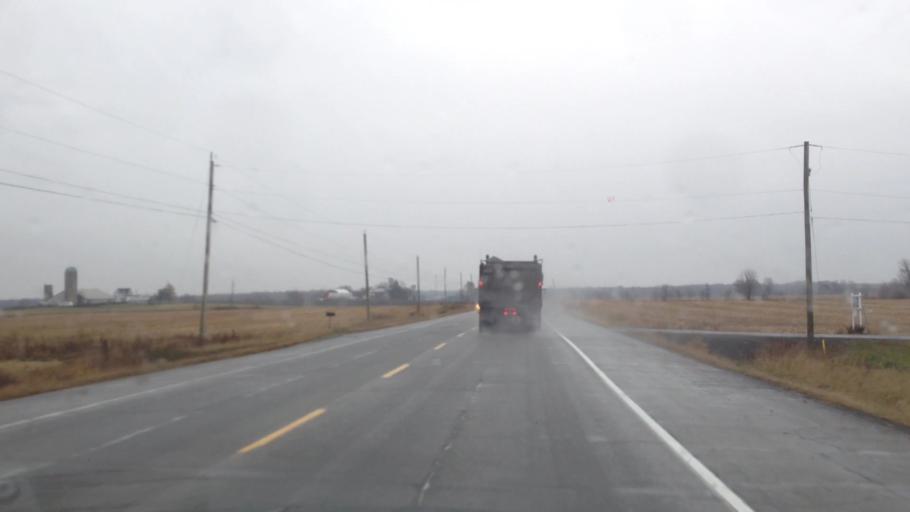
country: CA
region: Ontario
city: Clarence-Rockland
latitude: 45.4103
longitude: -75.4019
